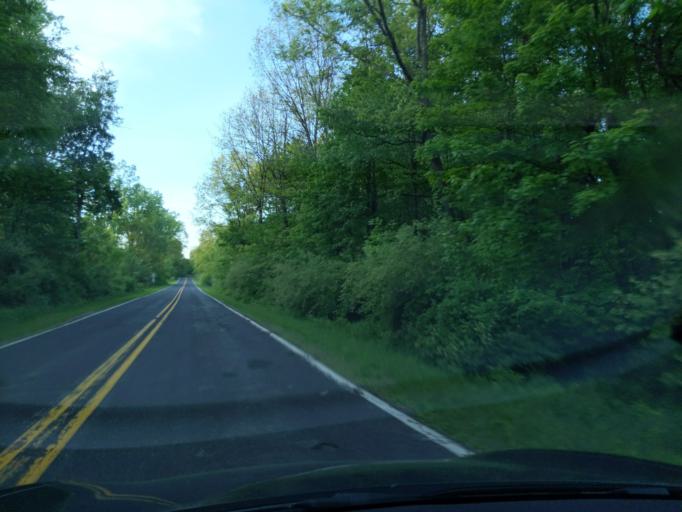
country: US
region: Michigan
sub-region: Ingham County
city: Leslie
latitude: 42.5040
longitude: -84.3119
